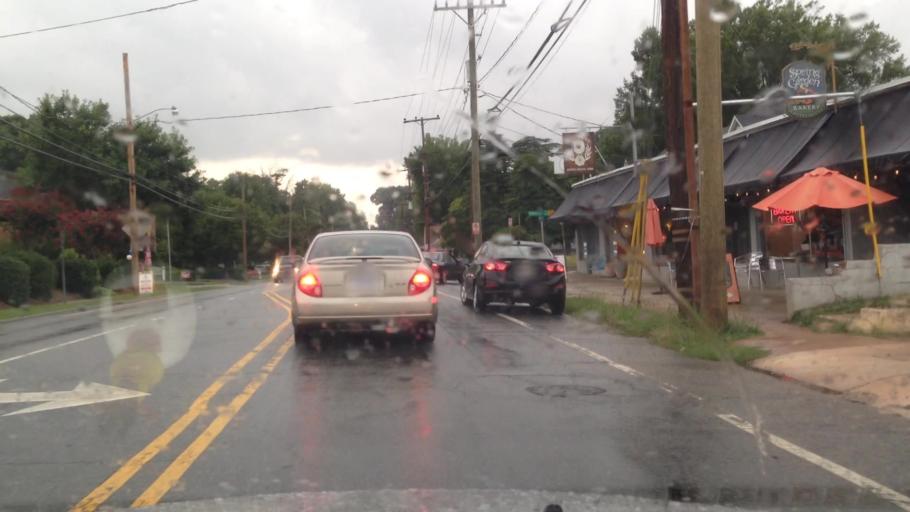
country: US
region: North Carolina
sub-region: Guilford County
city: Greensboro
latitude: 36.0638
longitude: -79.8242
